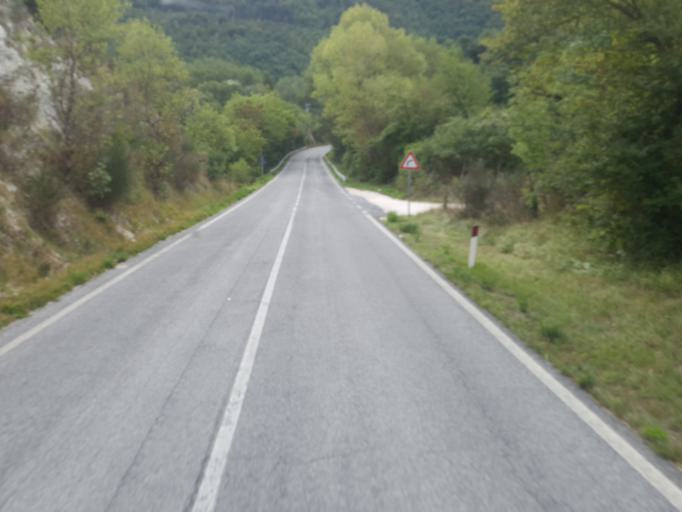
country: IT
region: The Marches
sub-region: Provincia di Ancona
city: Fabriano
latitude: 43.3232
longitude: 12.8356
